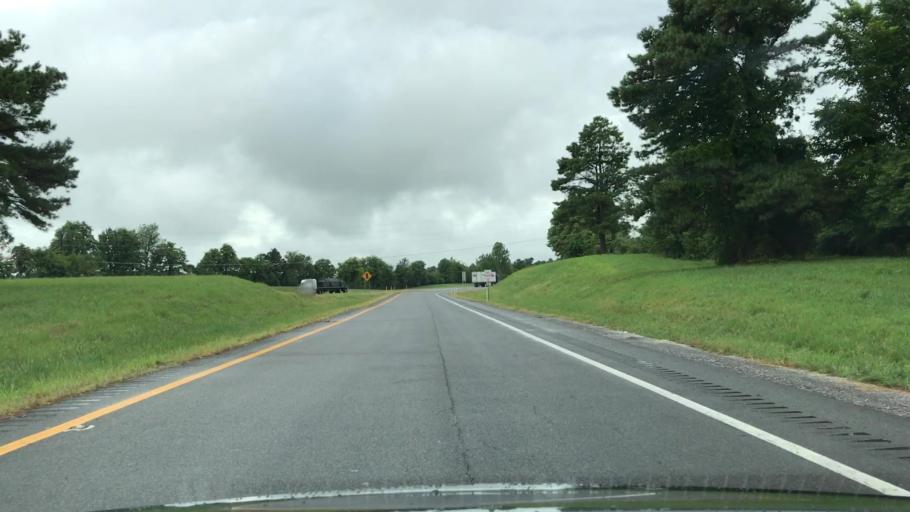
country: US
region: Kentucky
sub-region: Graves County
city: Mayfield
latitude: 36.7759
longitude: -88.5971
